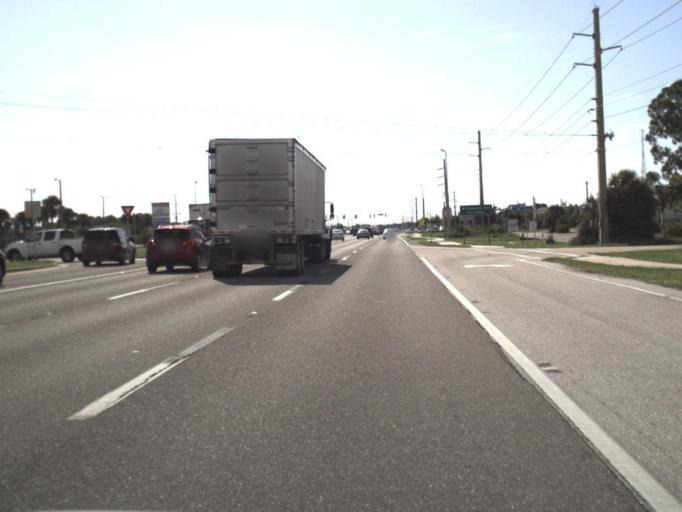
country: US
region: Florida
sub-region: Charlotte County
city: Port Charlotte
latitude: 26.9695
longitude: -82.0817
